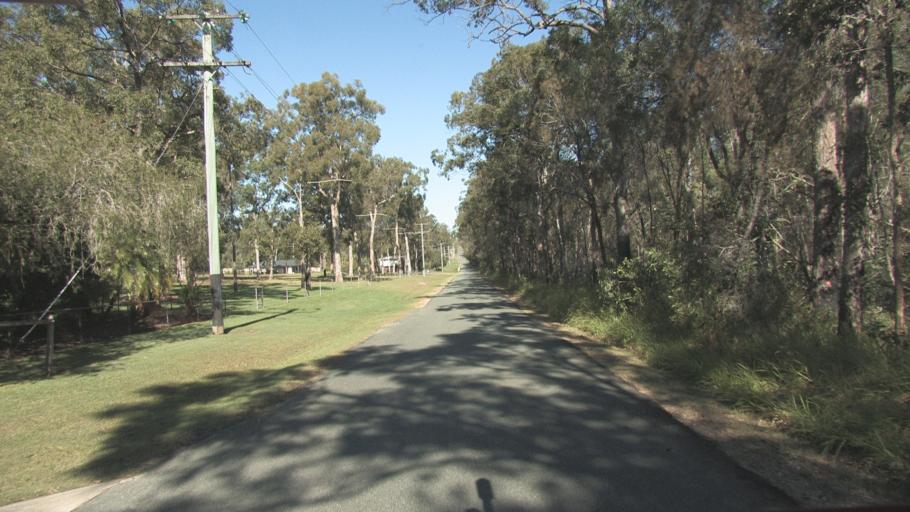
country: AU
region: Queensland
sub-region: Logan
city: Park Ridge South
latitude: -27.6939
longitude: 153.0049
